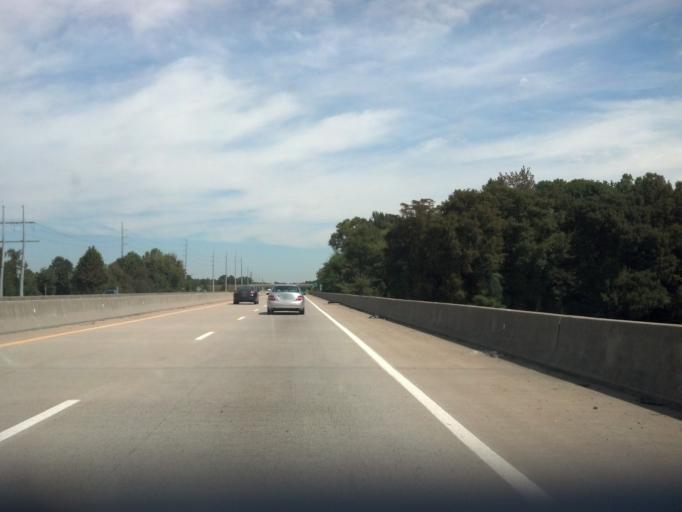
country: US
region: North Carolina
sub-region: Pitt County
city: Greenville
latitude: 35.6456
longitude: -77.4220
